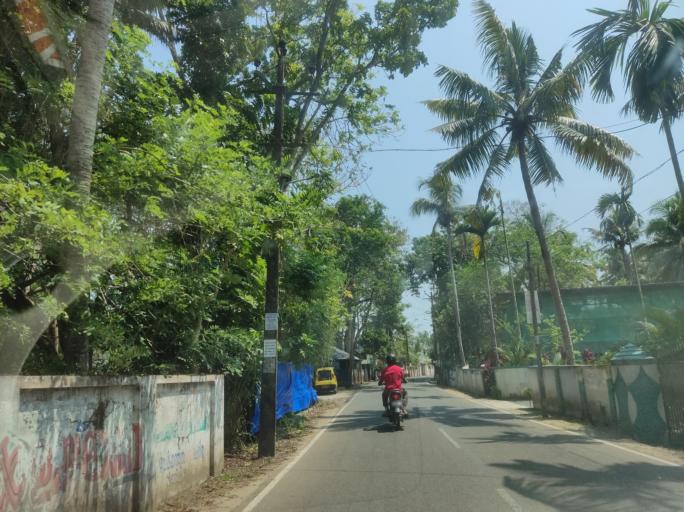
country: IN
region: Kerala
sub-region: Alappuzha
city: Kutiatodu
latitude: 9.7876
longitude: 76.3038
